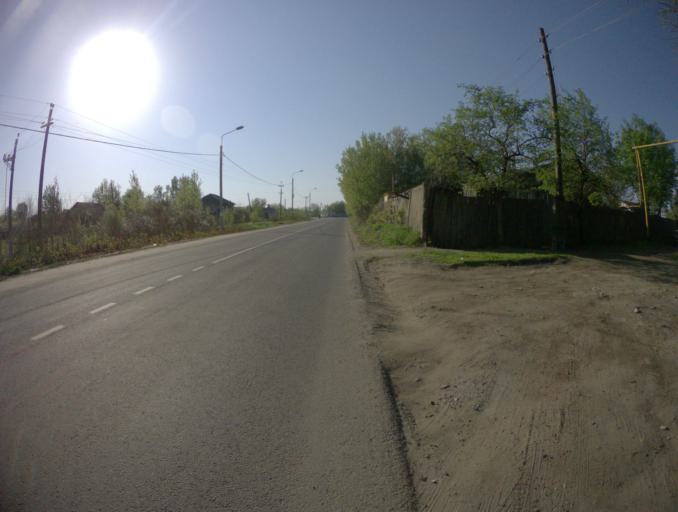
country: RU
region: Vladimir
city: Novovyazniki
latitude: 56.2035
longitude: 42.1679
